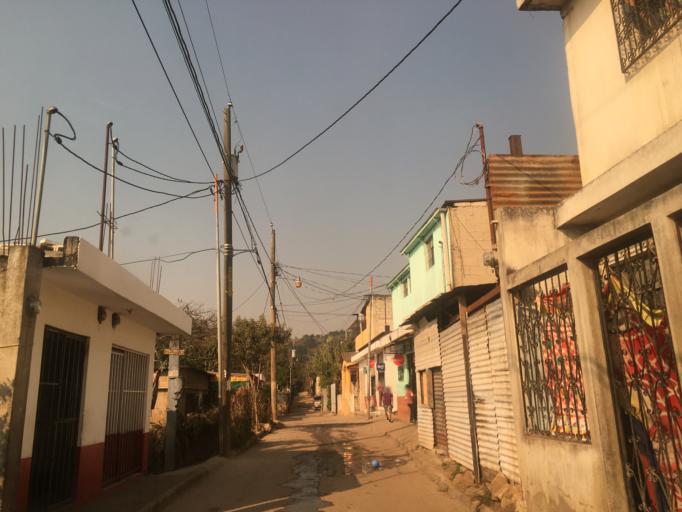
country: GT
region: Guatemala
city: Santa Catarina Pinula
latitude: 14.5430
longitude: -90.5046
